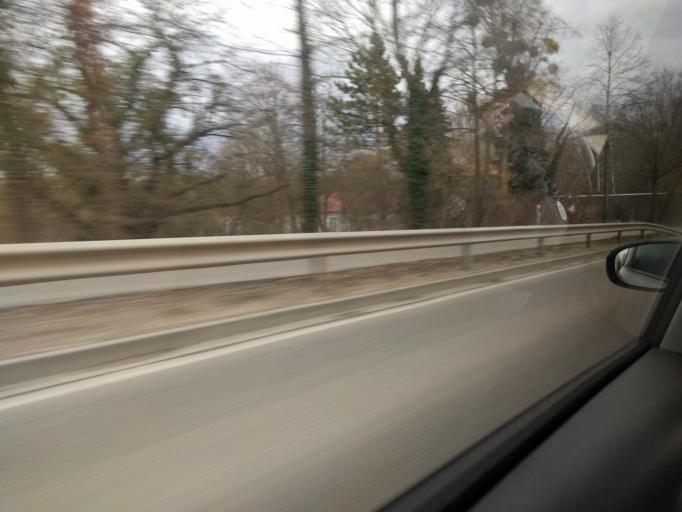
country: DE
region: Rheinland-Pfalz
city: Kuhardt
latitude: 49.1434
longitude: 8.3243
